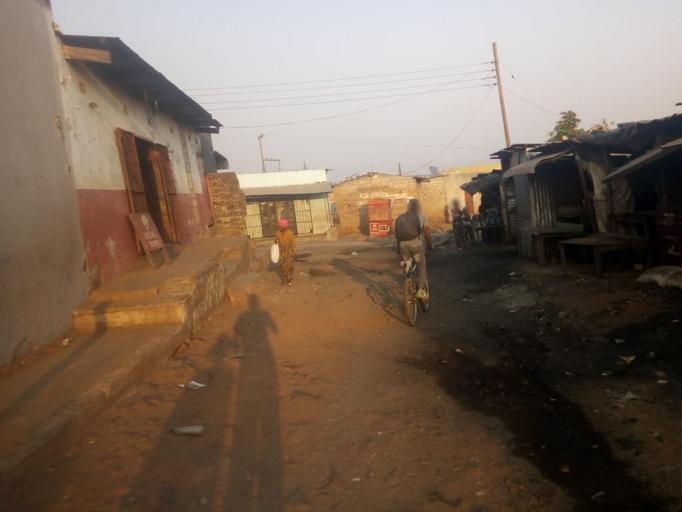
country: ZM
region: Lusaka
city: Lusaka
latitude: -15.4060
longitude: 28.3652
